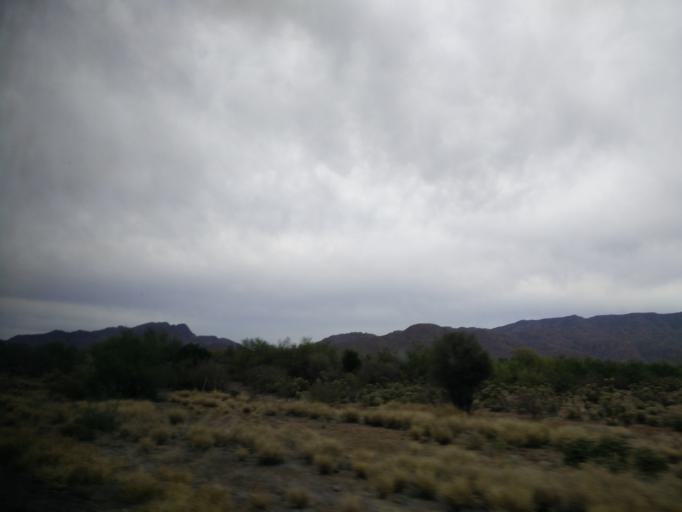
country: MX
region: Sonora
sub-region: Hermosillo
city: Miguel Aleman (La Doce)
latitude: 28.5556
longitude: -111.0371
